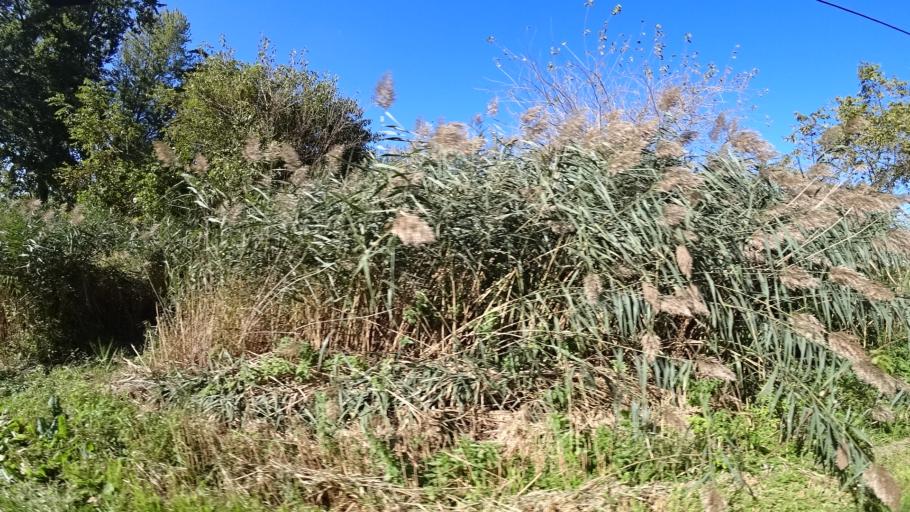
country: US
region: Indiana
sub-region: LaPorte County
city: Michigan City
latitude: 41.6772
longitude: -86.9133
